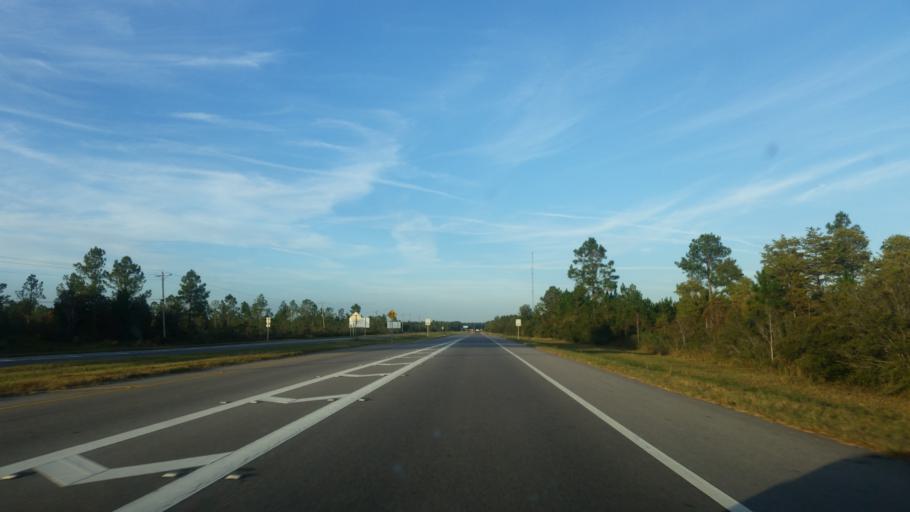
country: US
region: Alabama
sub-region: Mobile County
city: Grand Bay
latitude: 30.4583
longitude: -88.4169
